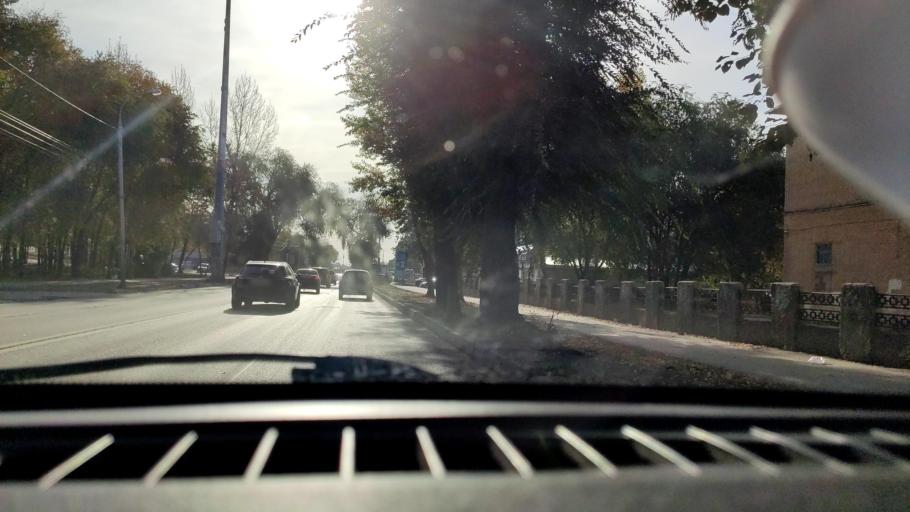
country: RU
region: Samara
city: Samara
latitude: 53.1943
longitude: 50.1384
